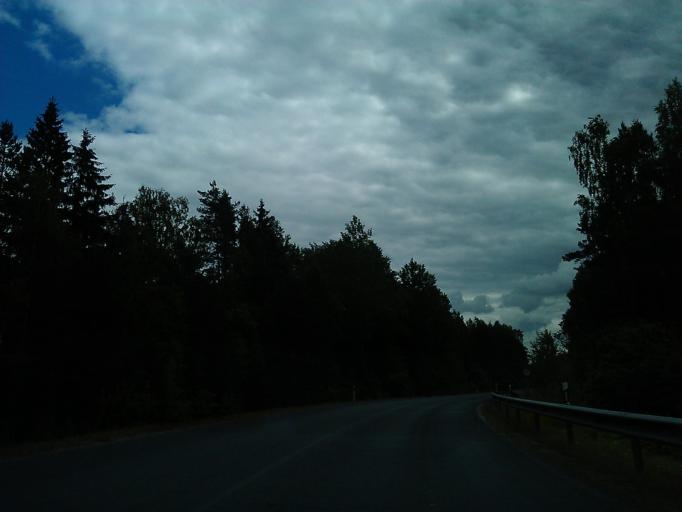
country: LV
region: Dobeles Rajons
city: Dobele
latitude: 56.6660
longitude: 23.1594
